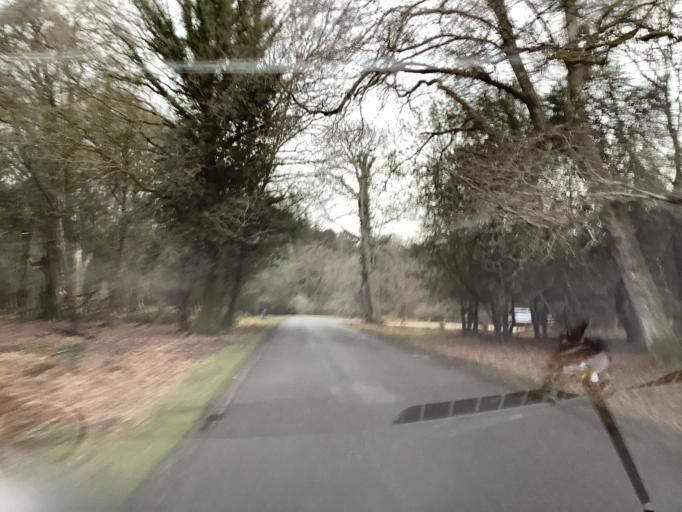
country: GB
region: England
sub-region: Hampshire
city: Lyndhurst
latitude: 50.8731
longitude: -1.6502
